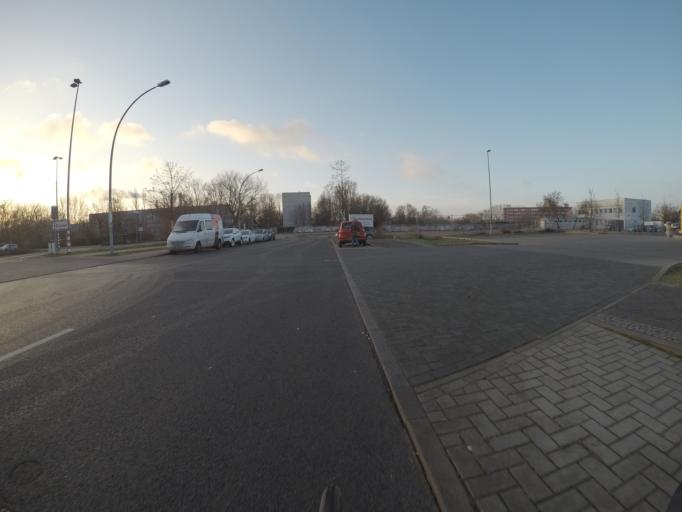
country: DE
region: Berlin
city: Rummelsburg
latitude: 52.4992
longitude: 13.4955
